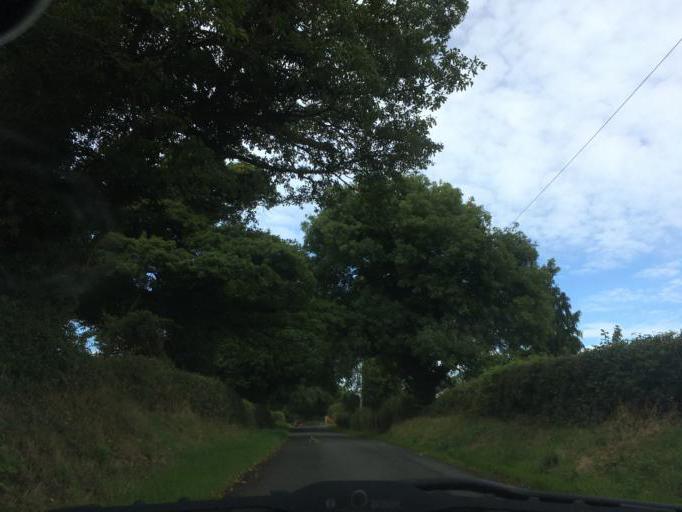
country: IE
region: Leinster
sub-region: Wicklow
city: Wicklow
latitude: 52.9178
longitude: -6.0937
